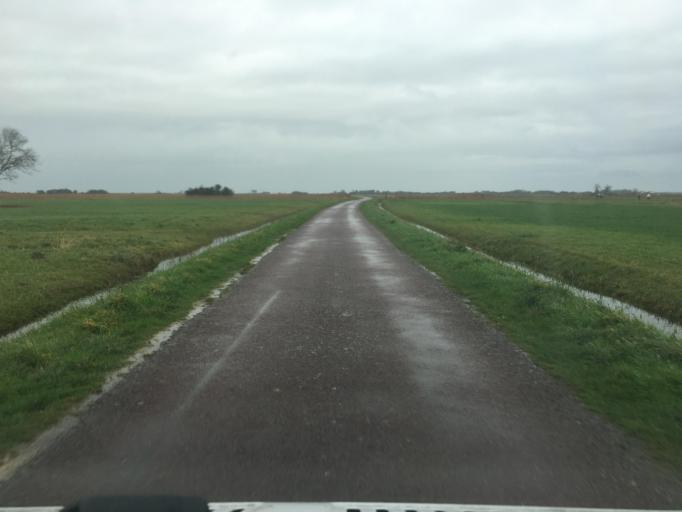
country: FR
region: Lower Normandy
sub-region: Departement de la Manche
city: Sainte-Mere-Eglise
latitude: 49.4460
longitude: -1.2380
